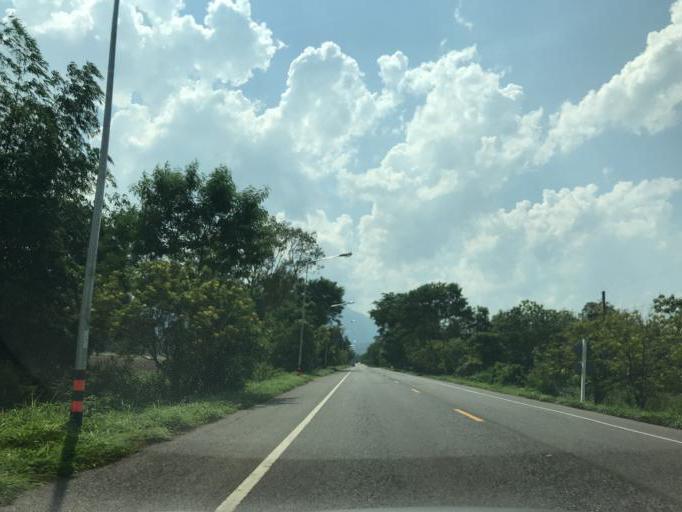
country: TH
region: Phayao
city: Phayao
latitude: 19.0819
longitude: 99.8613
